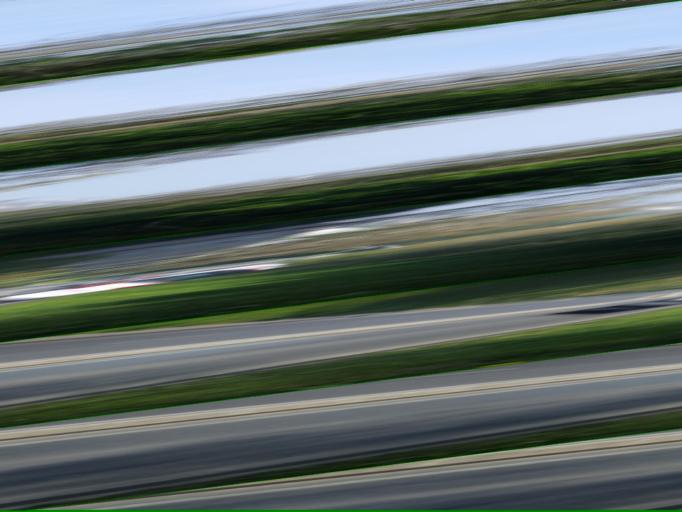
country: FR
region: Ile-de-France
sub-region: Departement de l'Essonne
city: La Ville-du-Bois
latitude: 48.6470
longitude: 2.2643
